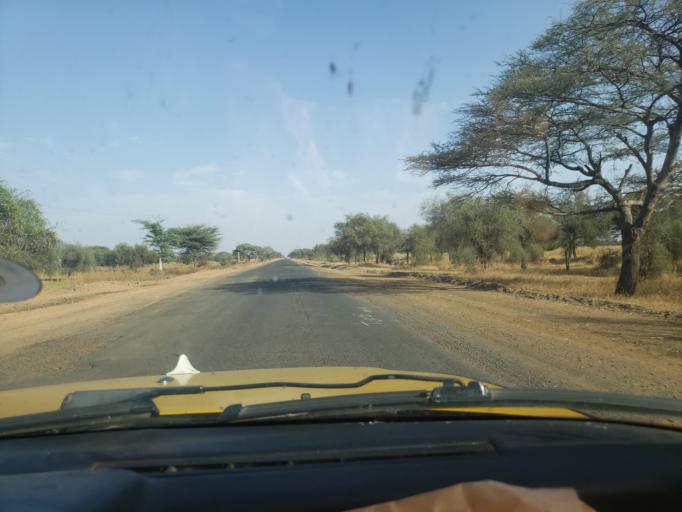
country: SN
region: Louga
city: Louga
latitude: 15.5067
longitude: -15.9657
